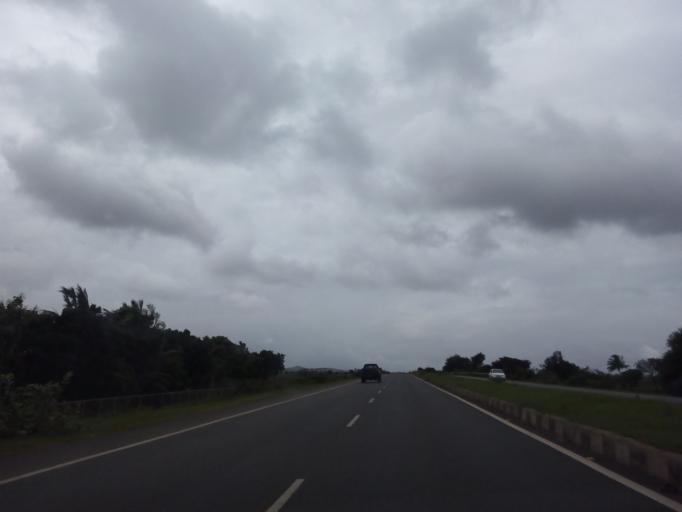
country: IN
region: Karnataka
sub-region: Haveri
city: Haveri
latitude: 14.7429
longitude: 75.4571
